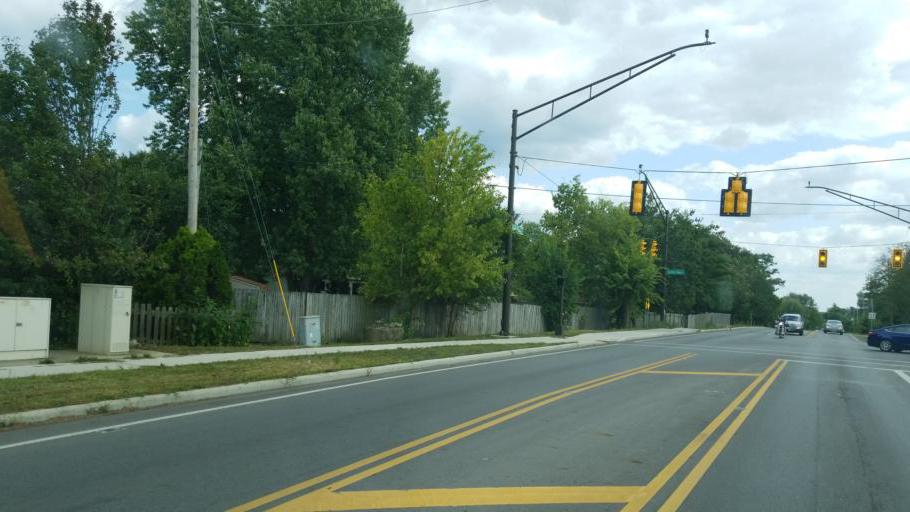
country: US
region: Ohio
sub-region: Delaware County
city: Powell
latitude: 40.1328
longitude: -83.0707
